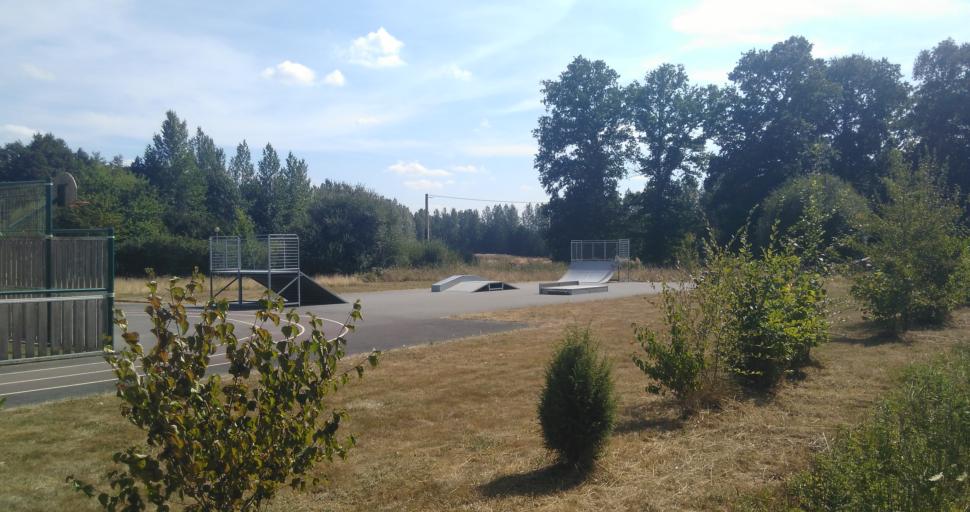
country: FR
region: Brittany
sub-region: Departement d'Ille-et-Vilaine
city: Geveze
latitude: 48.2146
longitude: -1.7853
